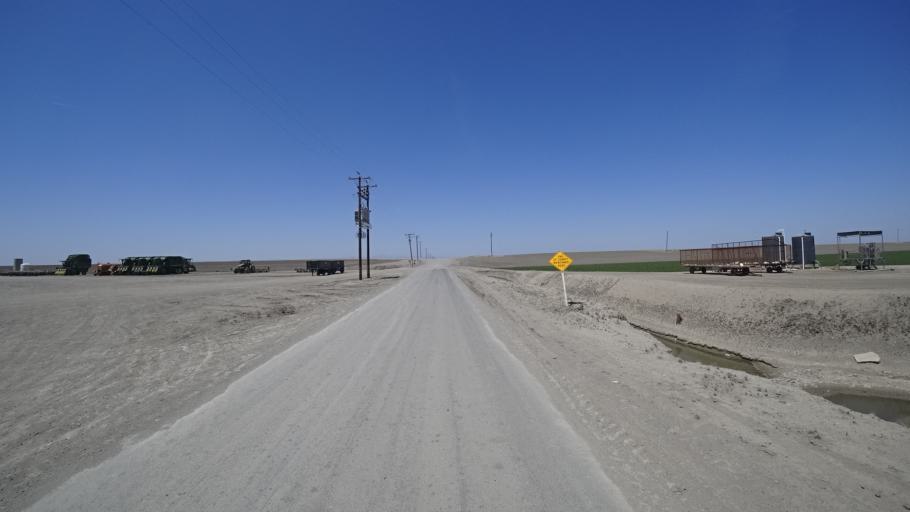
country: US
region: California
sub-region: Kings County
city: Corcoran
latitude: 36.0213
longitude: -119.6942
